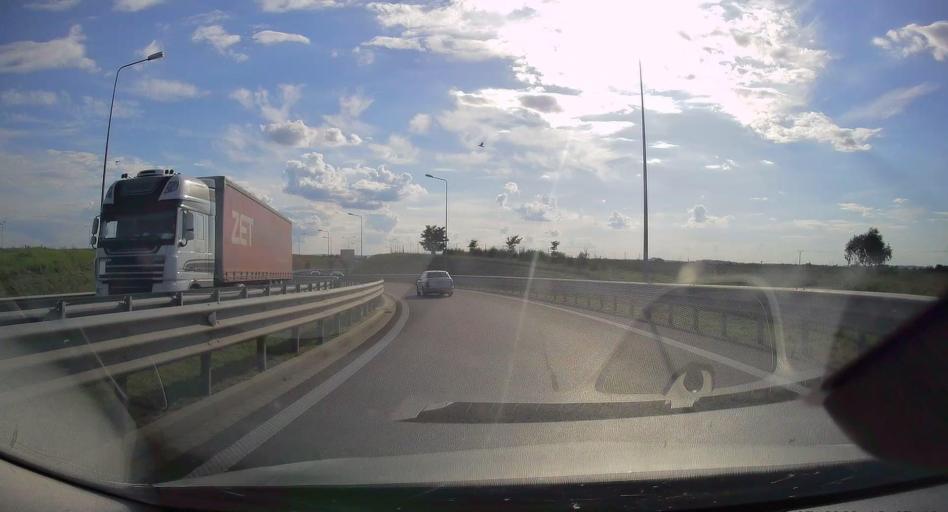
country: PL
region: Subcarpathian Voivodeship
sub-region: Powiat jaroslawski
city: Radymno
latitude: 49.9133
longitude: 22.8085
